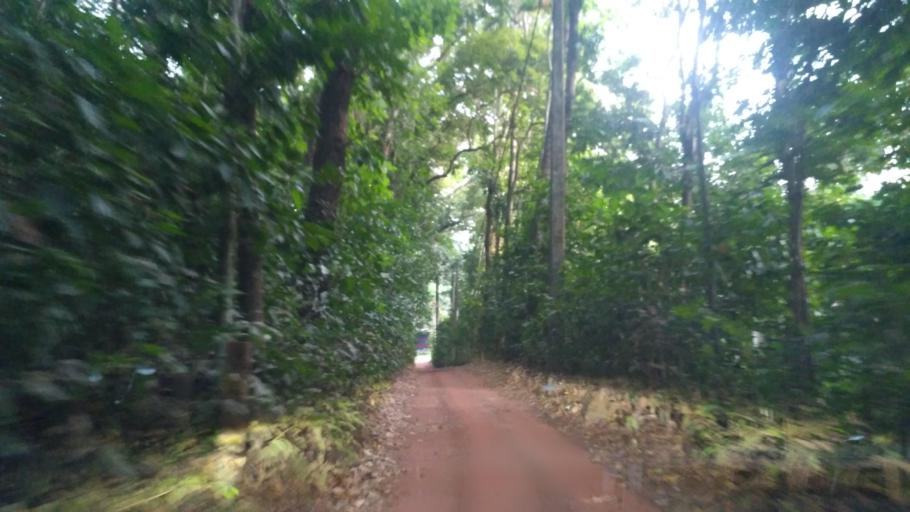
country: LK
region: North Western
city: Kuliyapitiya
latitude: 7.3343
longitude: 80.0048
